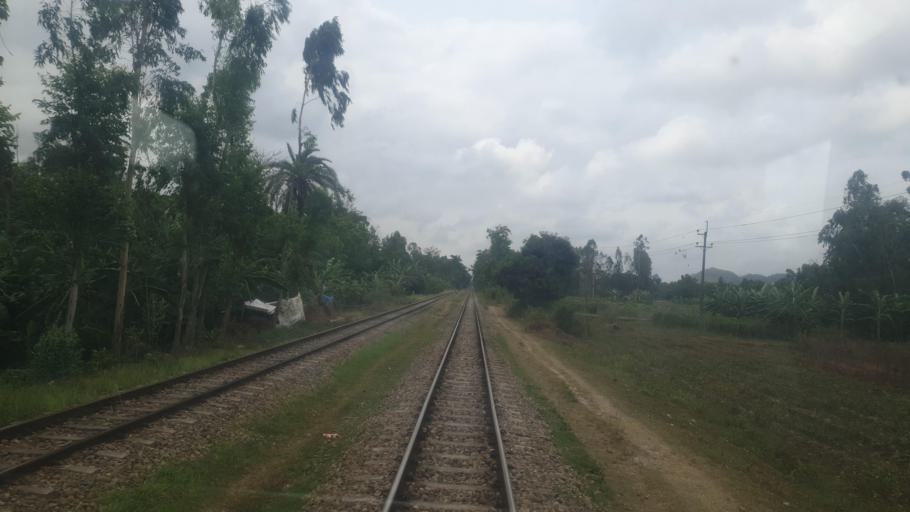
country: BD
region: Chittagong
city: Fatikchari
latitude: 22.6406
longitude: 91.6522
